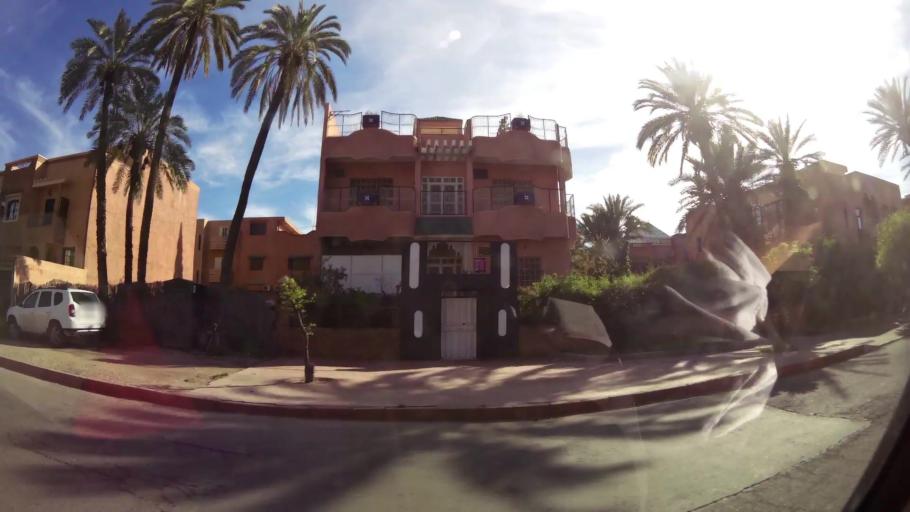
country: MA
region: Marrakech-Tensift-Al Haouz
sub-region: Marrakech
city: Marrakesh
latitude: 31.6567
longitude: -8.0139
